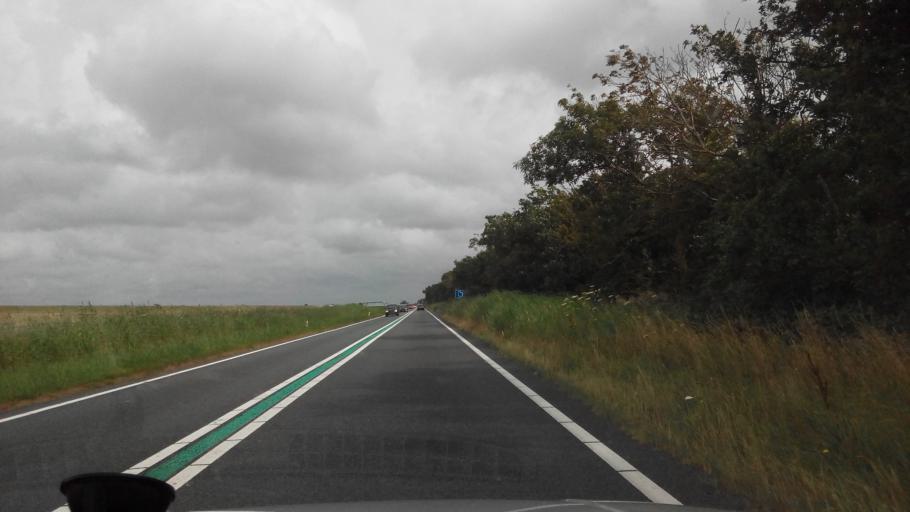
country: NL
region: North Holland
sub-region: Gemeente Schagen
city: Schagen
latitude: 52.8911
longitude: 4.8593
